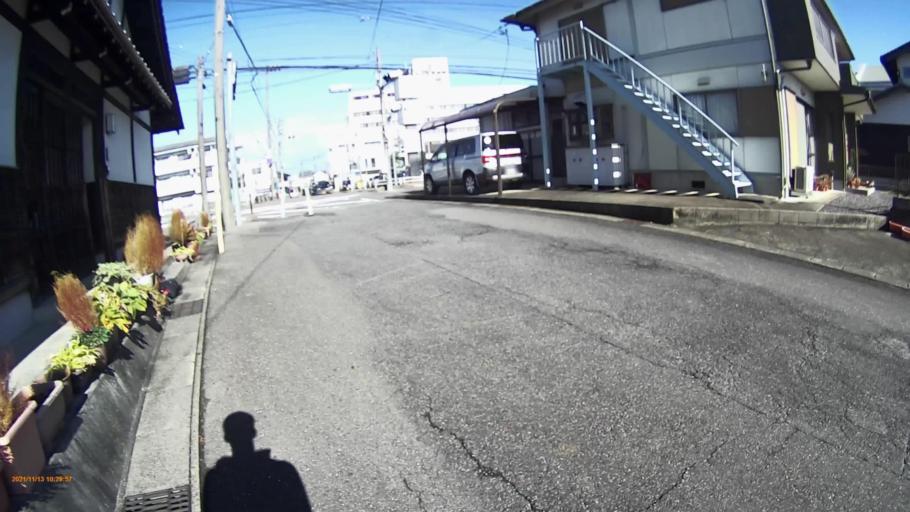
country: JP
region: Gifu
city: Minokamo
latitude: 35.4395
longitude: 137.0230
